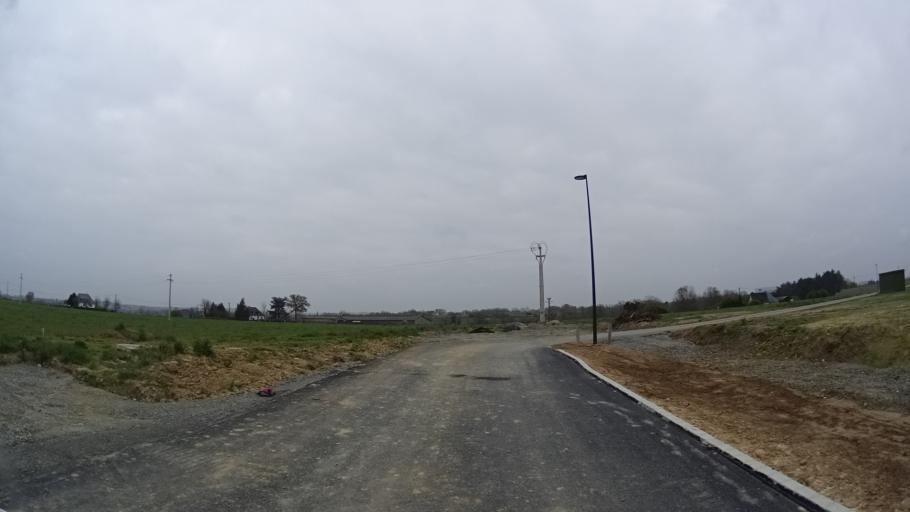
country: FR
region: Brittany
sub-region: Departement d'Ille-et-Vilaine
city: Brece
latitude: 48.1060
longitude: -1.4755
